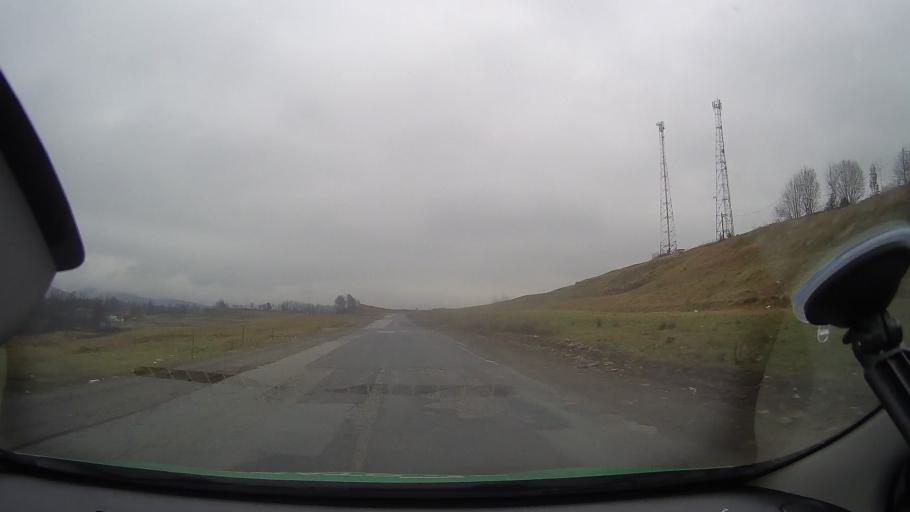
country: RO
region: Arad
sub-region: Comuna Halmagiu
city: Halmagiu
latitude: 46.2820
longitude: 22.5775
